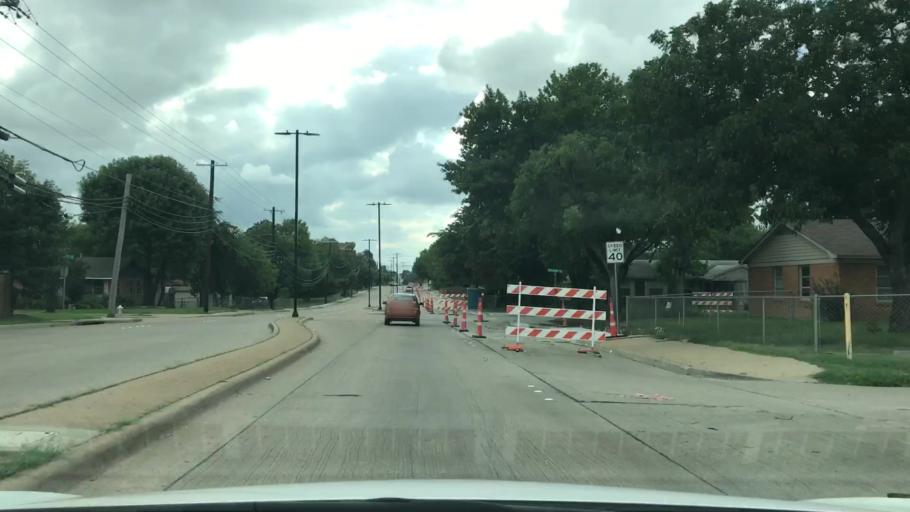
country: US
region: Texas
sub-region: Dallas County
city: Garland
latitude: 32.8944
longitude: -96.6314
